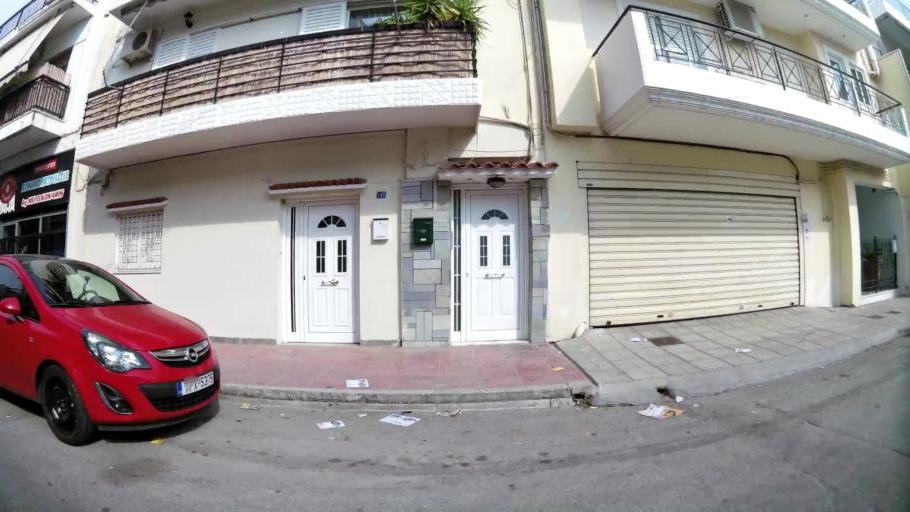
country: GR
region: Attica
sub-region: Nomarchia Athinas
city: Peristeri
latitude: 38.0167
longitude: 23.6808
